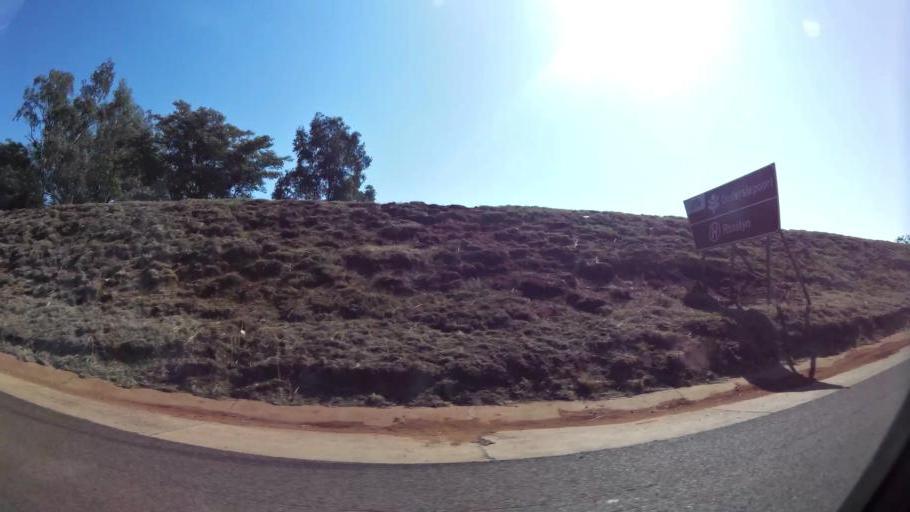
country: ZA
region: Gauteng
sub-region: City of Tshwane Metropolitan Municipality
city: Pretoria
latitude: -25.6489
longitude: 28.1426
